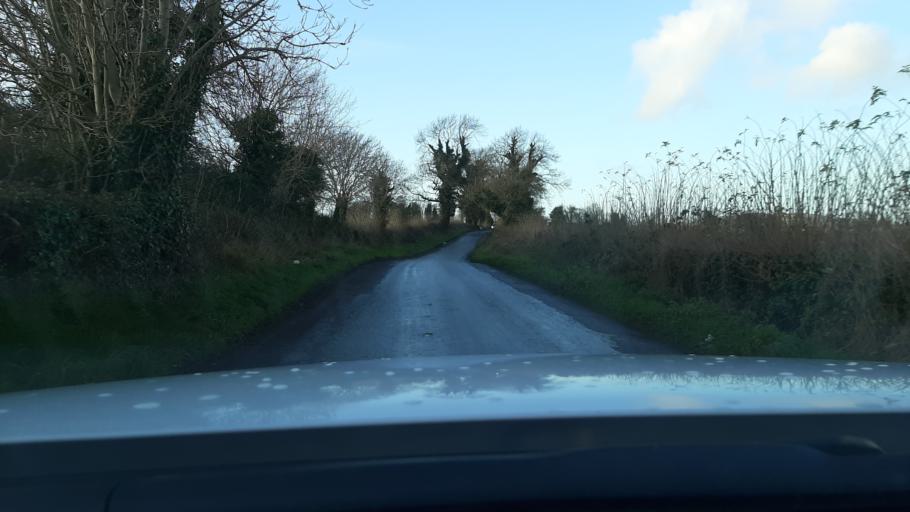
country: IE
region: Leinster
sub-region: Kildare
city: Kildare
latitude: 53.1656
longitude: -6.9217
